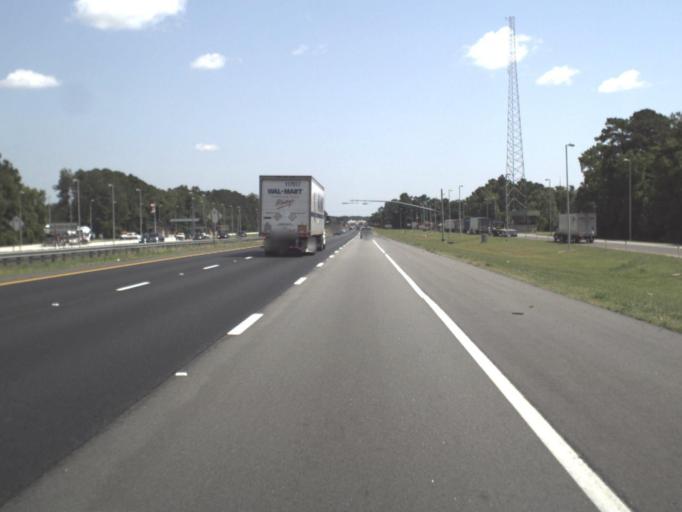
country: US
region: Georgia
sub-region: Camden County
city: Kingsland
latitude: 30.7239
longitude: -81.6648
